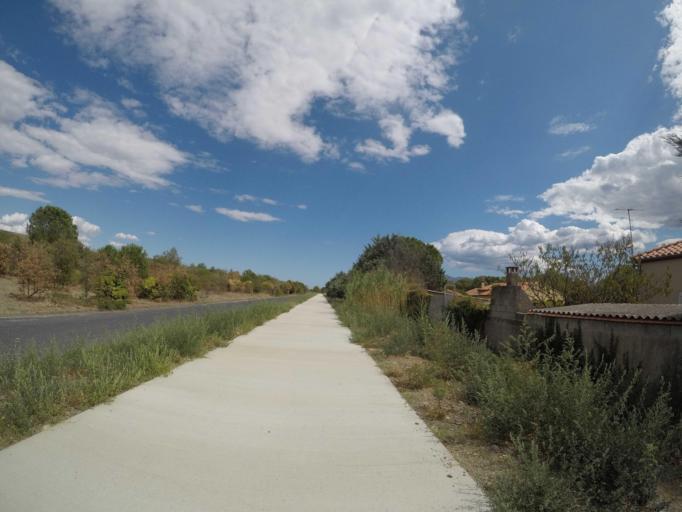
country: FR
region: Languedoc-Roussillon
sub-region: Departement des Pyrenees-Orientales
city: Ceret
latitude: 42.4991
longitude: 2.7497
